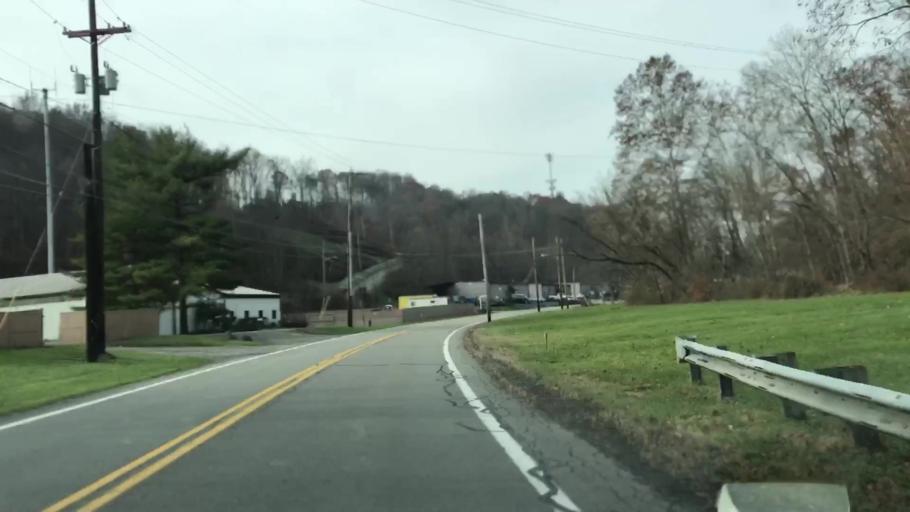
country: US
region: Pennsylvania
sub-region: Allegheny County
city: Carnot-Moon
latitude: 40.5305
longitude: -80.2318
